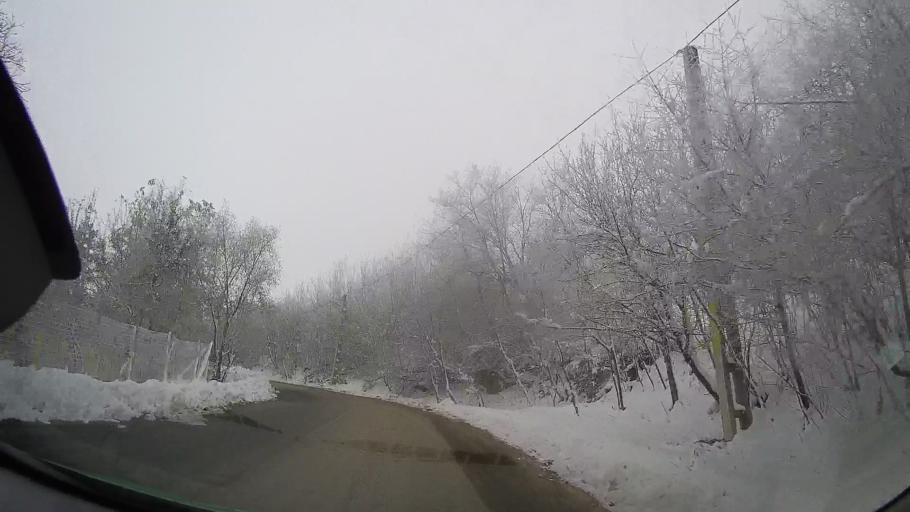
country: RO
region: Iasi
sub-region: Comuna Tansa
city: Suhulet
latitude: 46.8931
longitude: 27.2788
